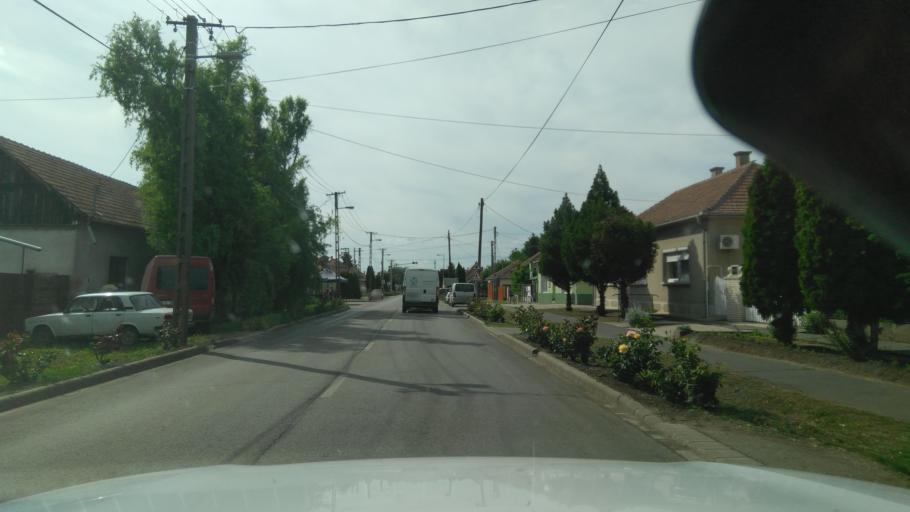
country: HU
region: Bekes
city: Medgyesegyhaza
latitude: 46.5002
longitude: 21.0243
